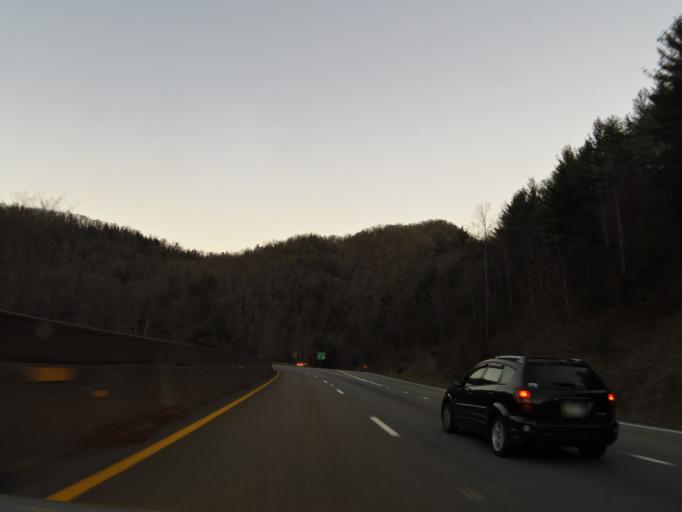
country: US
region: North Carolina
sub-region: Haywood County
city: Cove Creek
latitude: 35.7352
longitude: -83.0243
